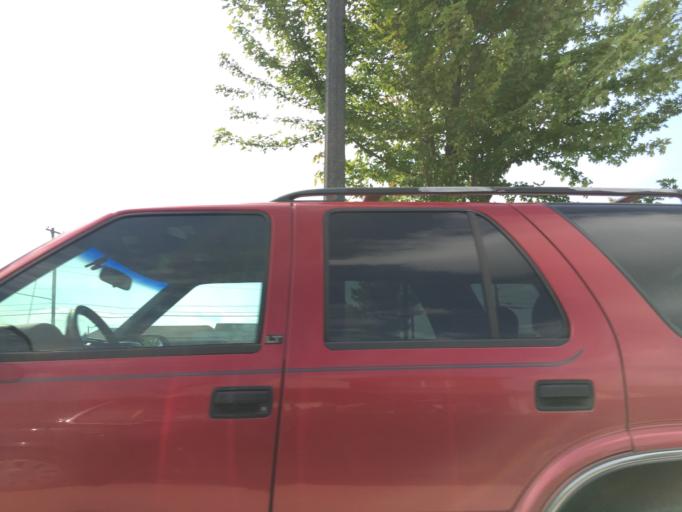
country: US
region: Michigan
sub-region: Wayne County
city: Grosse Pointe Park
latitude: 42.3640
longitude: -82.9731
